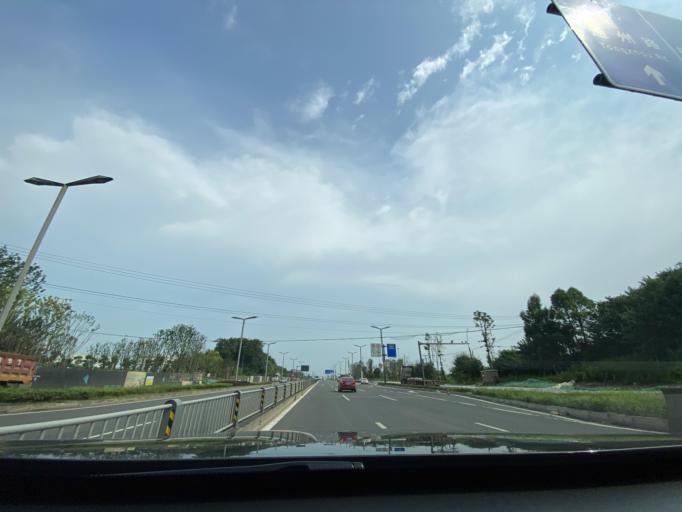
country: CN
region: Sichuan
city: Longquan
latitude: 30.4435
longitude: 104.0953
